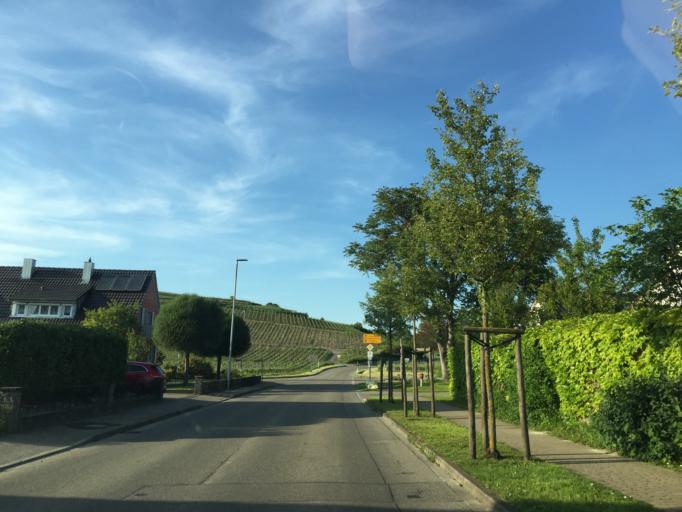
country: DE
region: Baden-Wuerttemberg
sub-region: Freiburg Region
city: Vogtsburg
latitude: 48.0918
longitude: 7.6259
